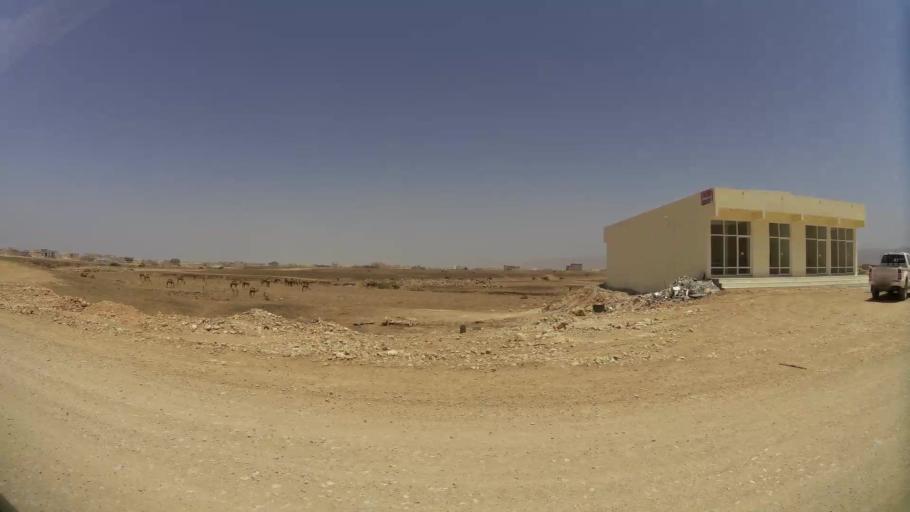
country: OM
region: Zufar
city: Salalah
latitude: 17.0971
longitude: 54.2056
